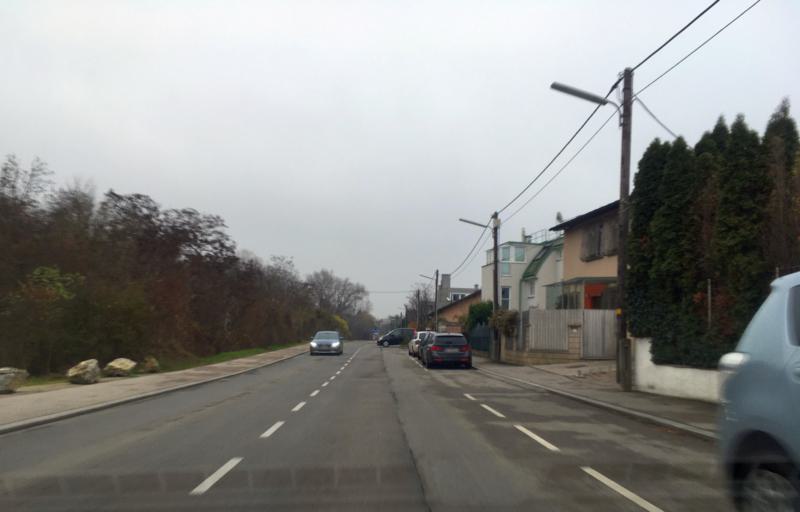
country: AT
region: Vienna
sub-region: Wien Stadt
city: Vienna
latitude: 48.2132
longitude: 16.4518
